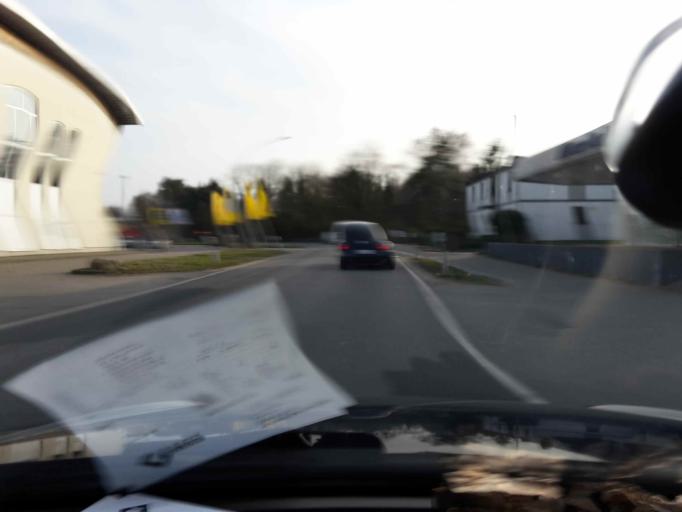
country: DE
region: Lower Saxony
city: Buchholz in der Nordheide
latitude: 53.3159
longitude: 9.8792
